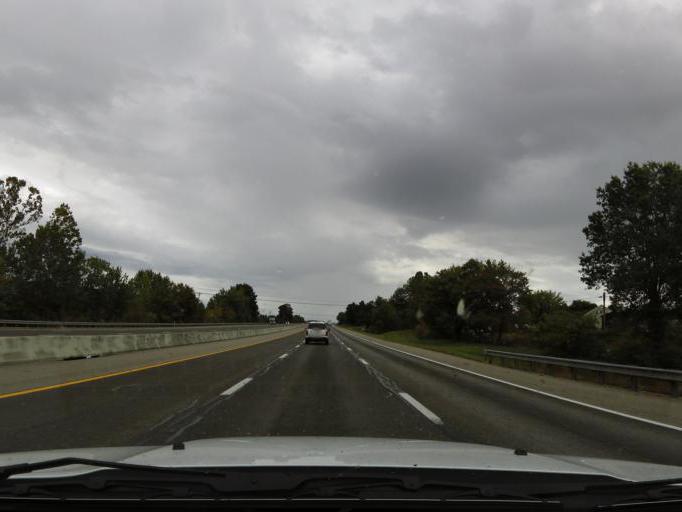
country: US
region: Kentucky
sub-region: Laurel County
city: London
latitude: 37.0757
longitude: -84.0991
